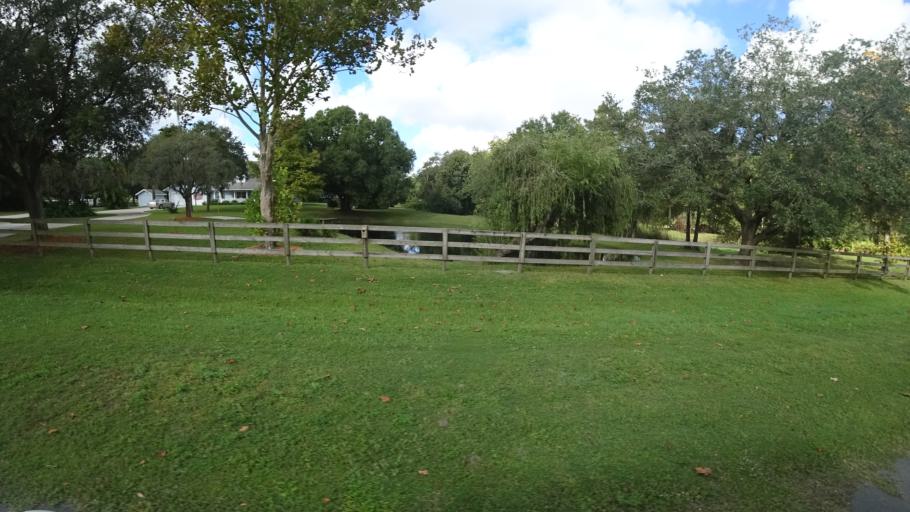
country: US
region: Florida
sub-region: Sarasota County
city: Lake Sarasota
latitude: 27.3674
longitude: -82.2503
